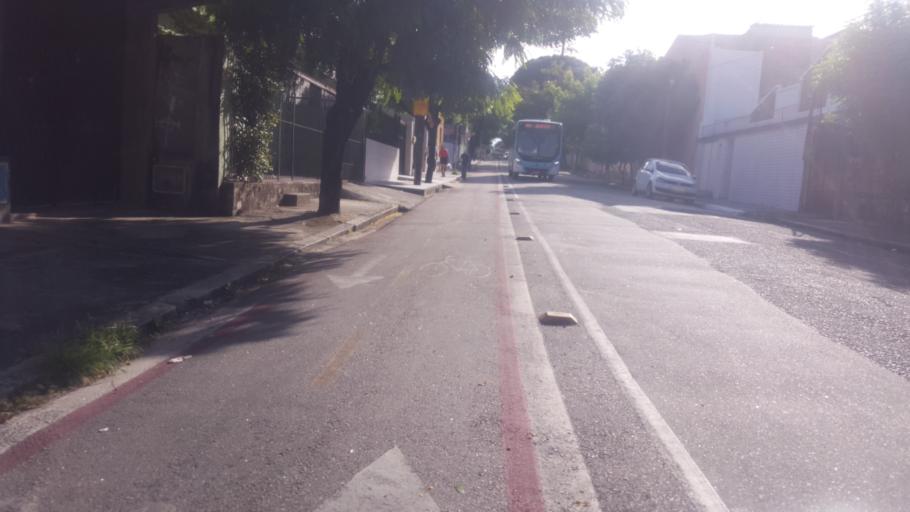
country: BR
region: Ceara
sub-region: Fortaleza
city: Fortaleza
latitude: -3.7451
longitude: -38.5400
